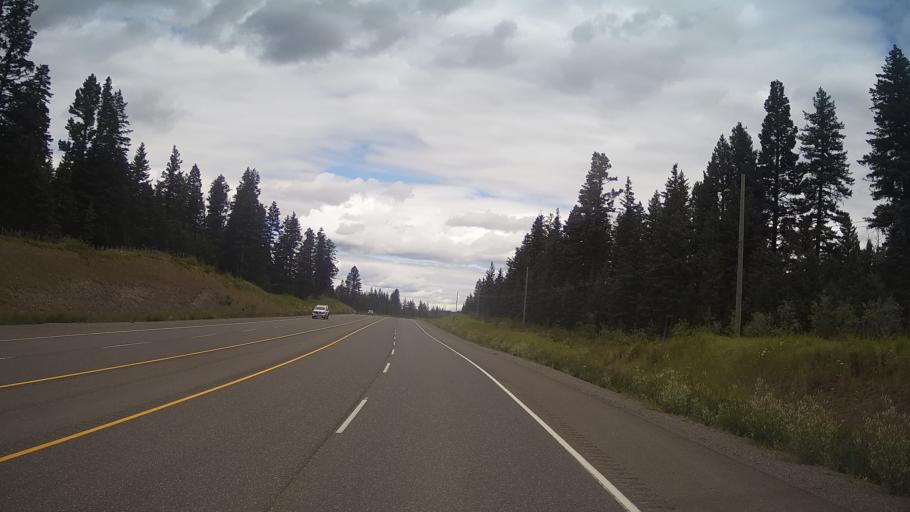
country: CA
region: British Columbia
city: Cache Creek
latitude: 51.4097
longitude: -121.3755
